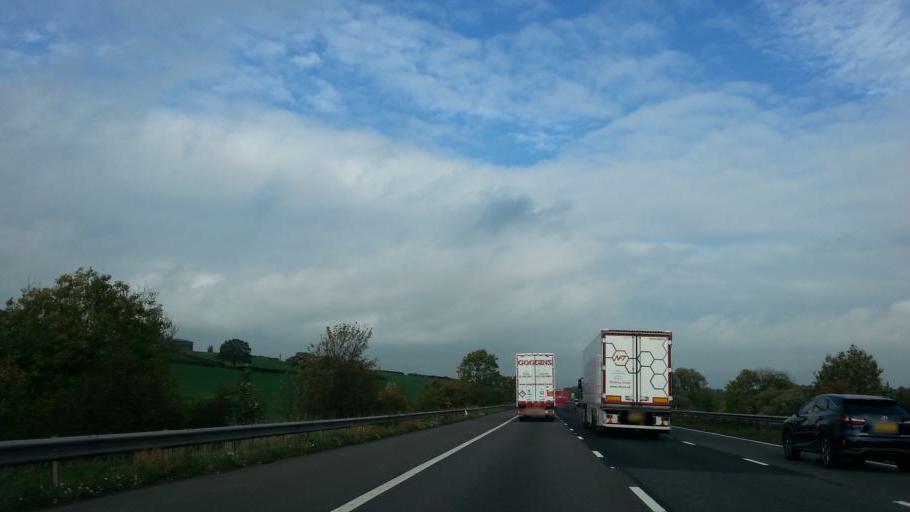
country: GB
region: England
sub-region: Staffordshire
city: Audley
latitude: 53.0363
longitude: -2.3296
